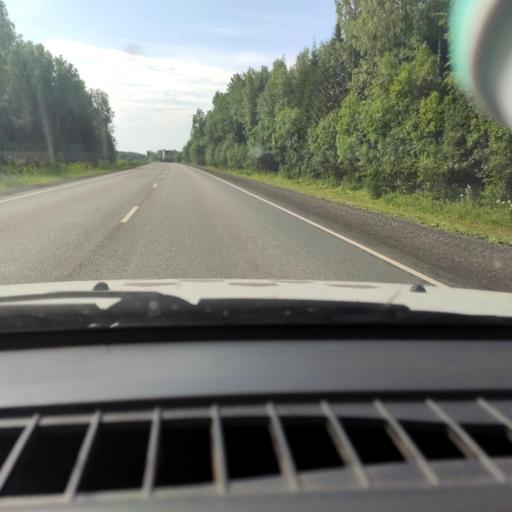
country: RU
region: Perm
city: Siva
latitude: 58.4991
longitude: 54.0460
